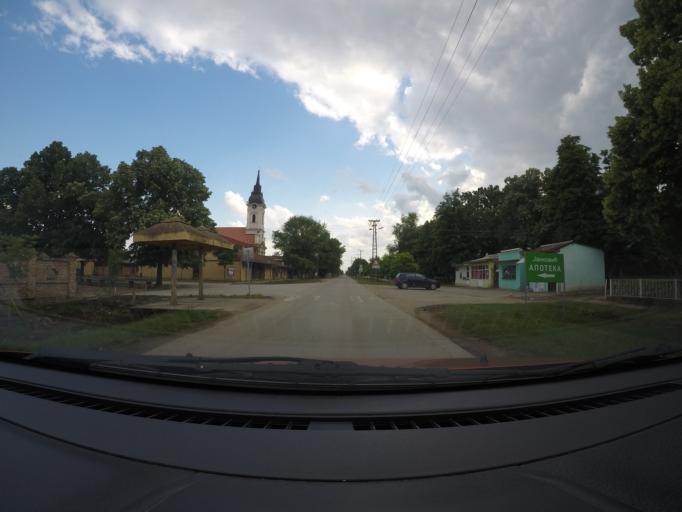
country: RS
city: Tomasevac
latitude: 45.2684
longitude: 20.6207
